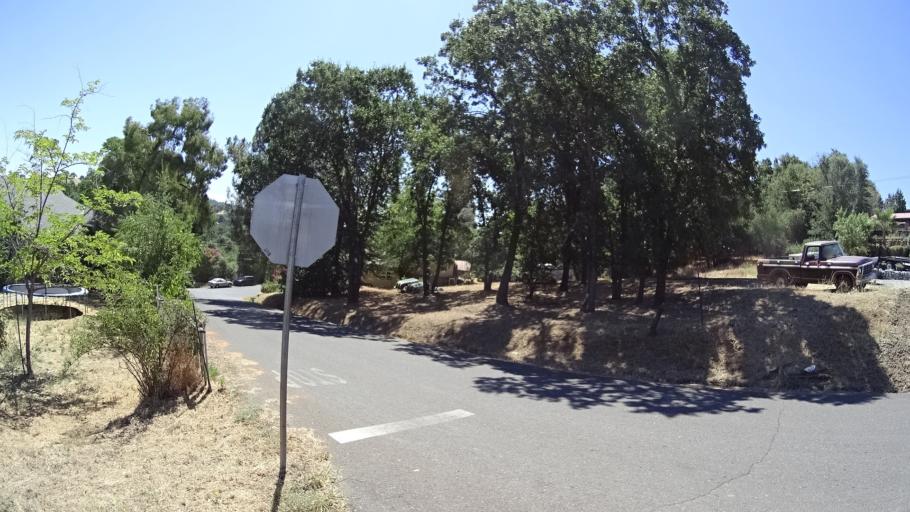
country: US
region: California
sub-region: Calaveras County
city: Angels Camp
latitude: 38.0742
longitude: -120.5414
